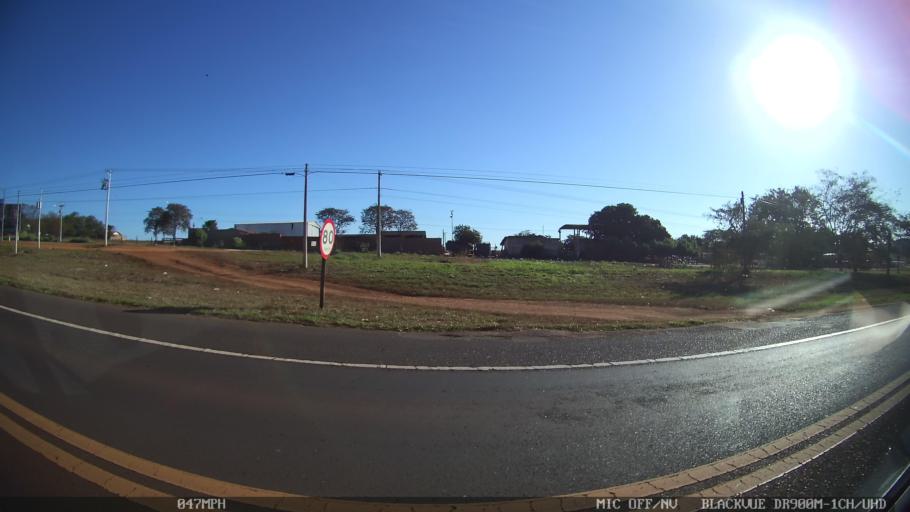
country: BR
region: Sao Paulo
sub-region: Olimpia
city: Olimpia
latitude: -20.6924
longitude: -48.9173
